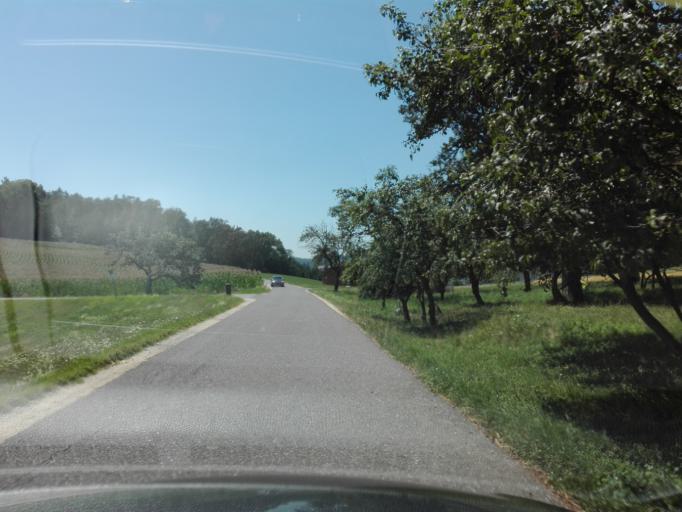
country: AT
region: Upper Austria
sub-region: Politischer Bezirk Urfahr-Umgebung
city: Engerwitzdorf
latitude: 48.3088
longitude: 14.4214
